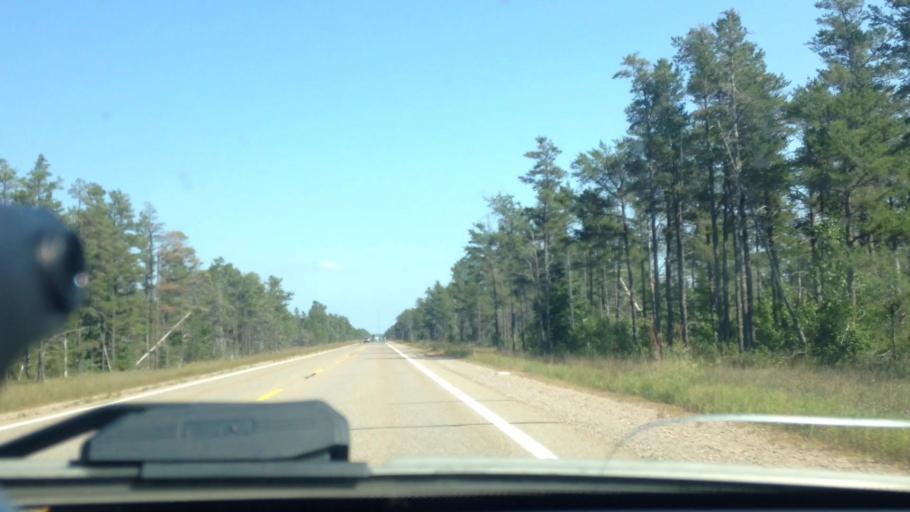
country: US
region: Michigan
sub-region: Mackinac County
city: Saint Ignace
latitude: 46.3586
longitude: -84.8378
